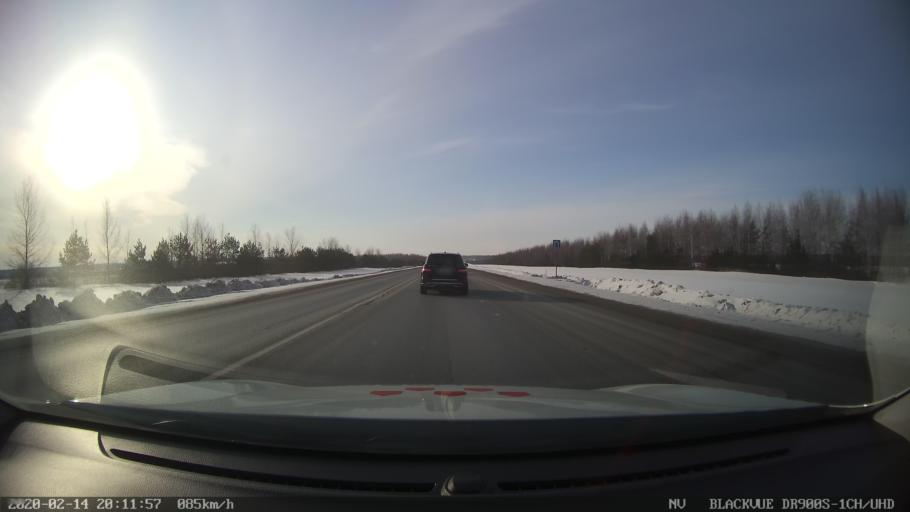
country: RU
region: Tatarstan
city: Verkhniy Uslon
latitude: 55.6714
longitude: 48.8678
